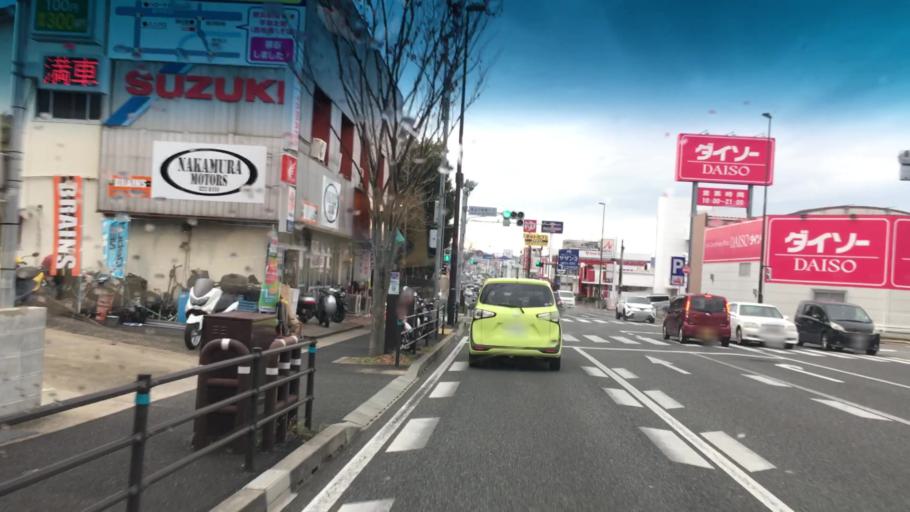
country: JP
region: Fukuoka
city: Fukuoka-shi
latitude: 33.5683
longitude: 130.3323
